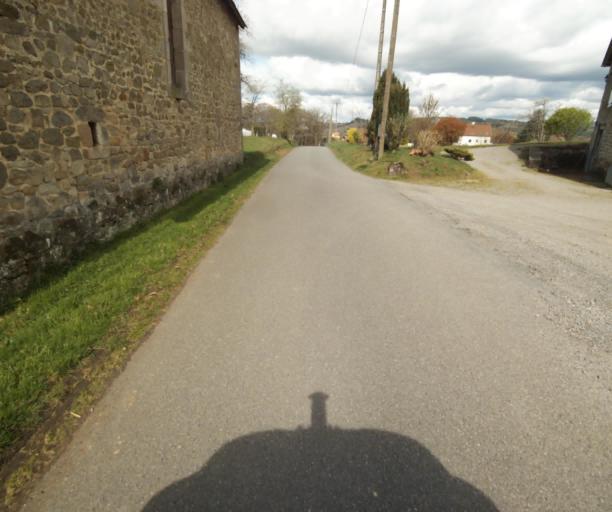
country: FR
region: Limousin
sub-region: Departement de la Correze
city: Correze
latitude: 45.3677
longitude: 1.8927
